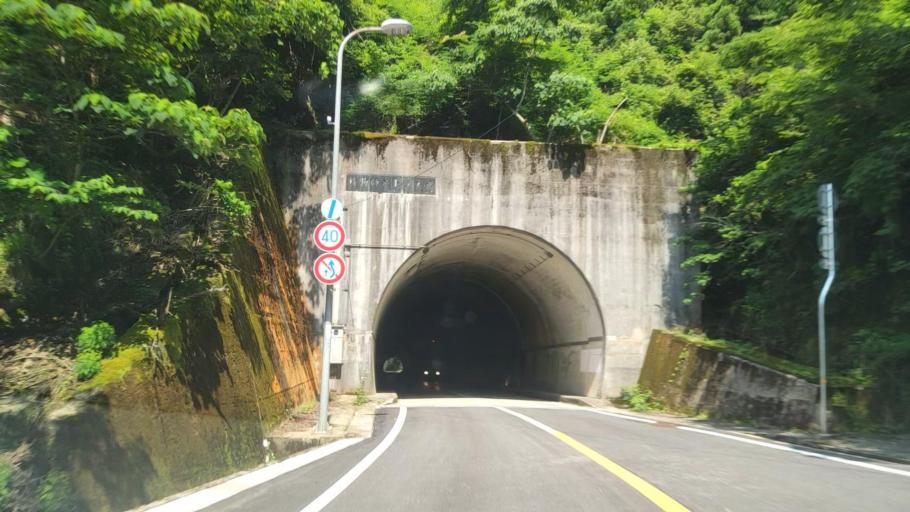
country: JP
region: Hyogo
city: Toyooka
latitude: 35.6371
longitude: 134.7787
